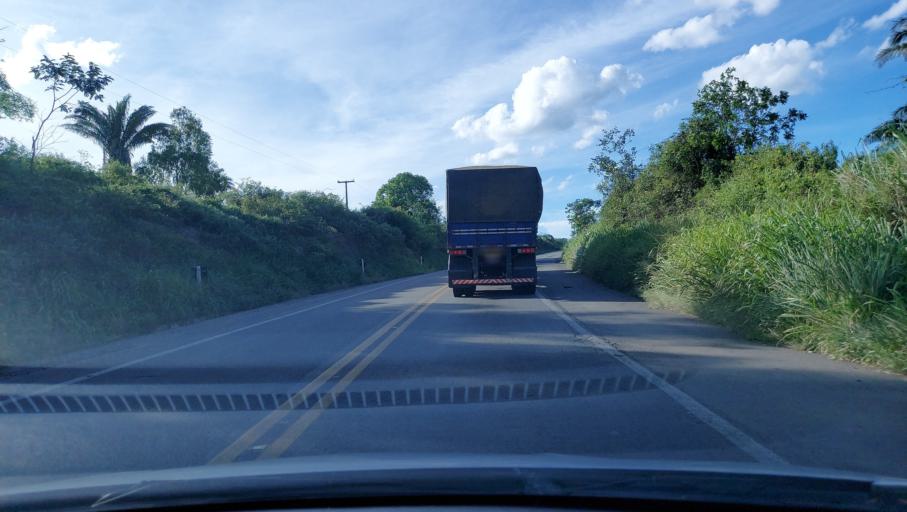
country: BR
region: Bahia
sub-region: Seabra
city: Seabra
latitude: -12.4085
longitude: -41.8699
